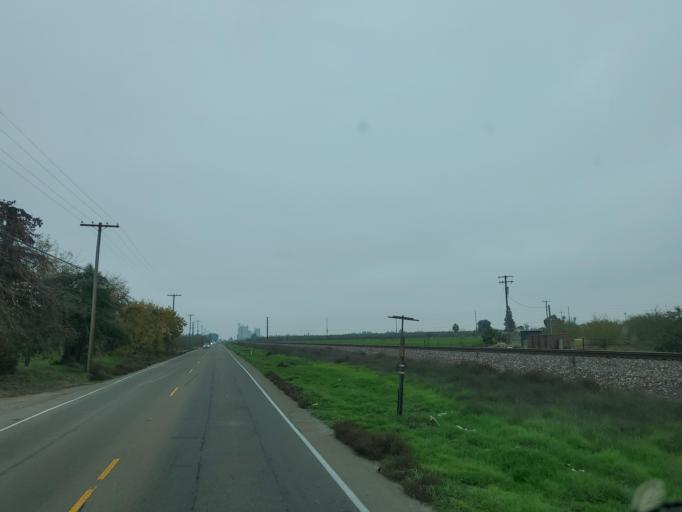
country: US
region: California
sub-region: Stanislaus County
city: Hughson
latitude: 37.5845
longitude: -120.8565
